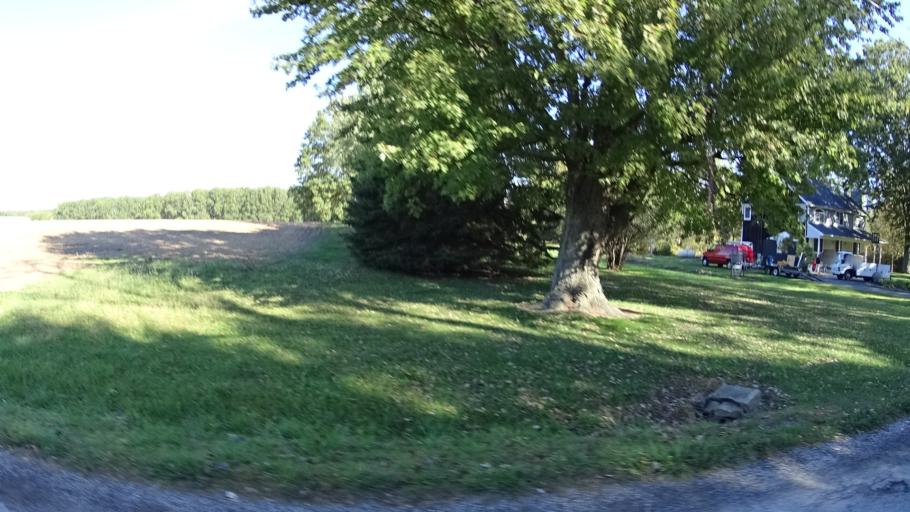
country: US
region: Ohio
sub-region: Lorain County
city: Vermilion-on-the-Lake
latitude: 41.3993
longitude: -82.3000
